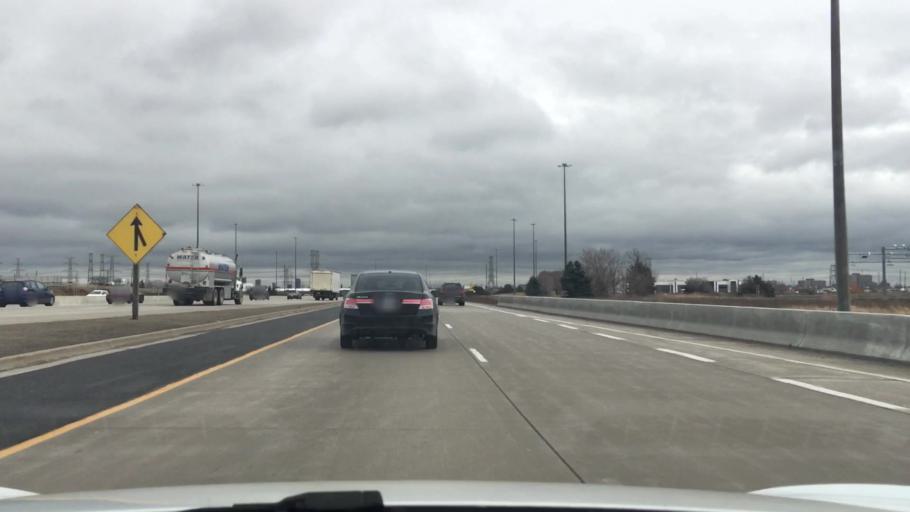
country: CA
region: Ontario
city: Etobicoke
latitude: 43.7561
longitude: -79.6239
